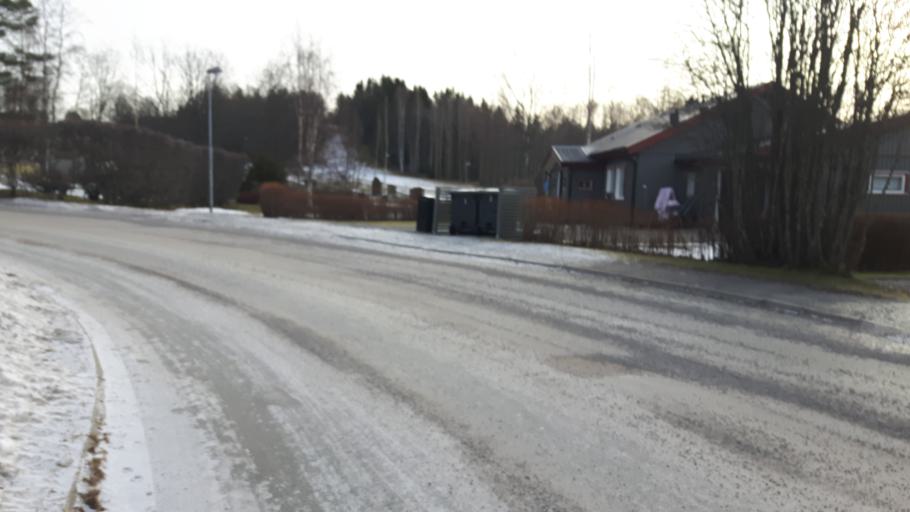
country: SE
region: Vaesternorrland
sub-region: Haernoesands Kommun
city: Haernoesand
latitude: 62.6312
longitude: 17.9648
